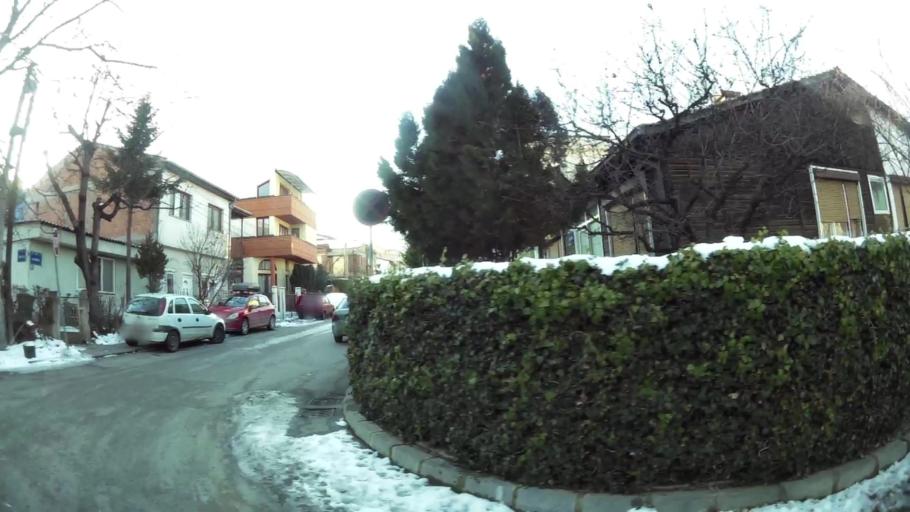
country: MK
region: Karpos
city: Skopje
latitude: 41.9922
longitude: 21.4025
